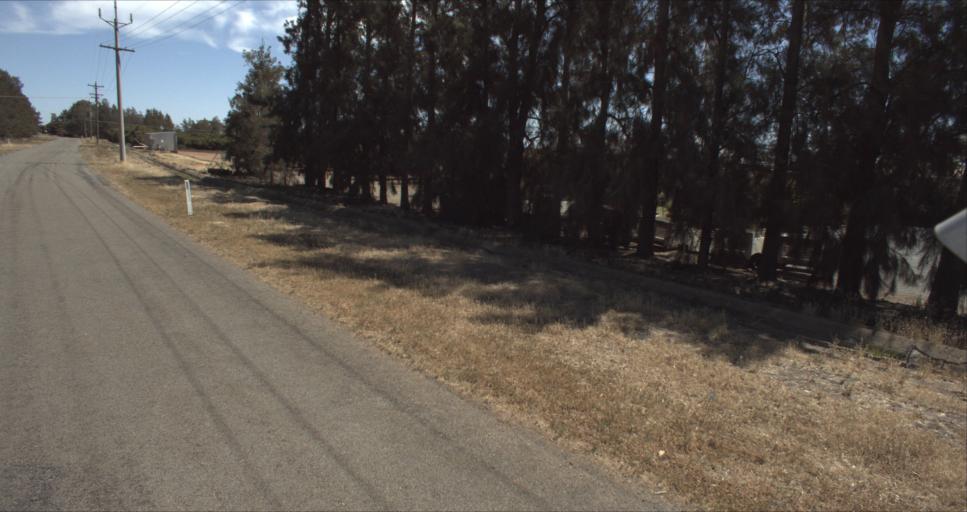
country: AU
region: New South Wales
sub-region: Leeton
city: Leeton
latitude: -34.5987
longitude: 146.4365
